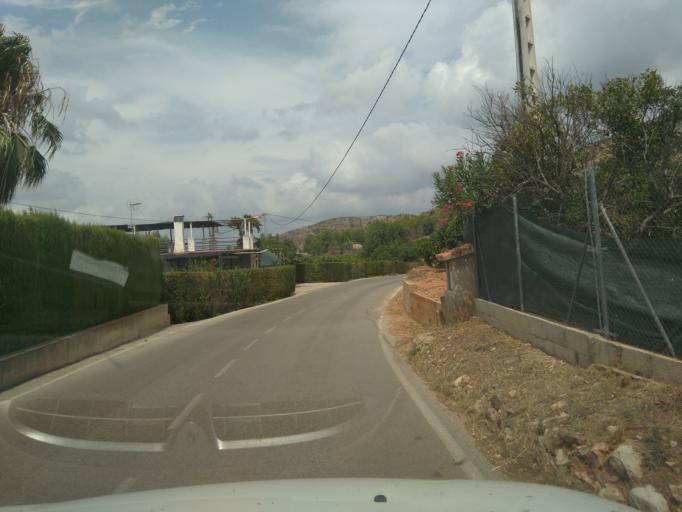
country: ES
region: Valencia
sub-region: Provincia de Valencia
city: La Pobla Llarga
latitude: 39.0843
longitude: -0.4236
